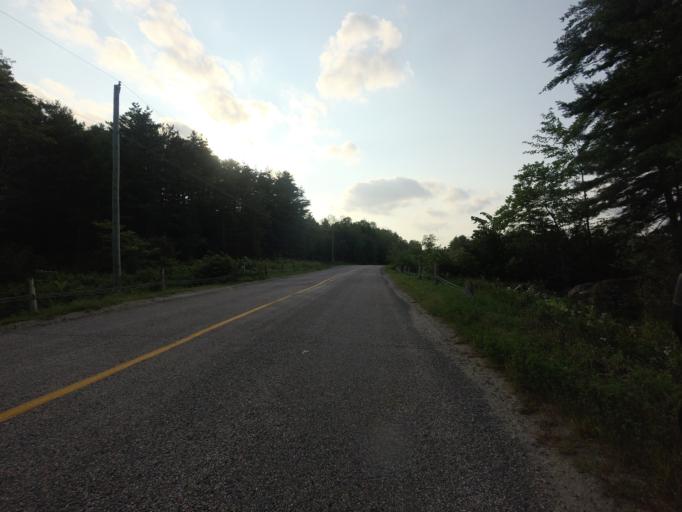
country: CA
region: Ontario
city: Perth
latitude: 44.9642
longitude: -76.6887
